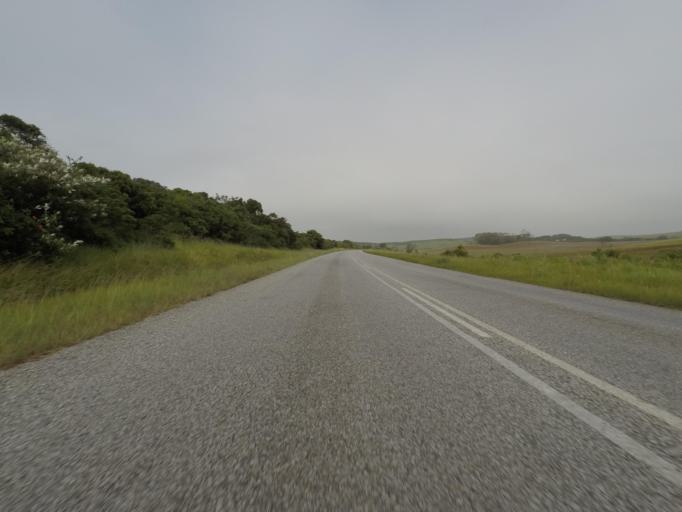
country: ZA
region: Eastern Cape
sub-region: Cacadu District Municipality
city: Port Alfred
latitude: -33.6064
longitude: 26.8255
